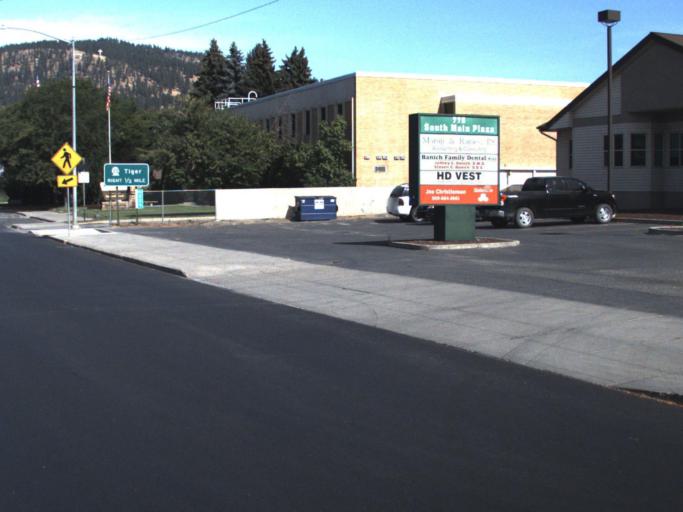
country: US
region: Washington
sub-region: Stevens County
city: Colville
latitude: 48.5373
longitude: -117.9057
